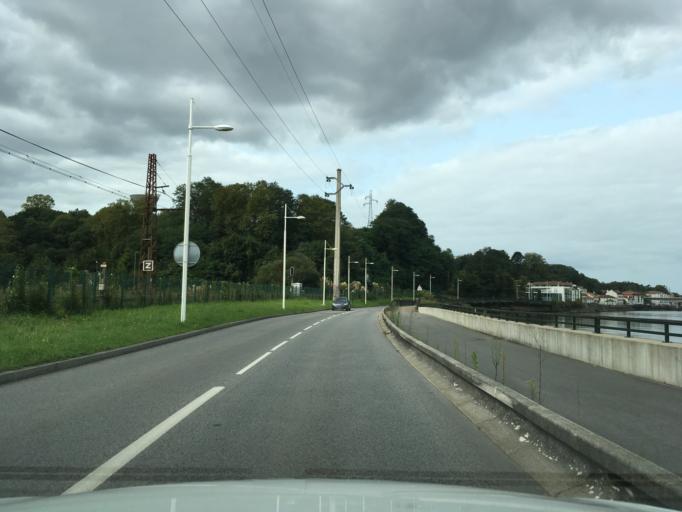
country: FR
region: Aquitaine
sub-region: Departement des Pyrenees-Atlantiques
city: Bayonne
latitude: 43.4836
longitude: -1.4538
